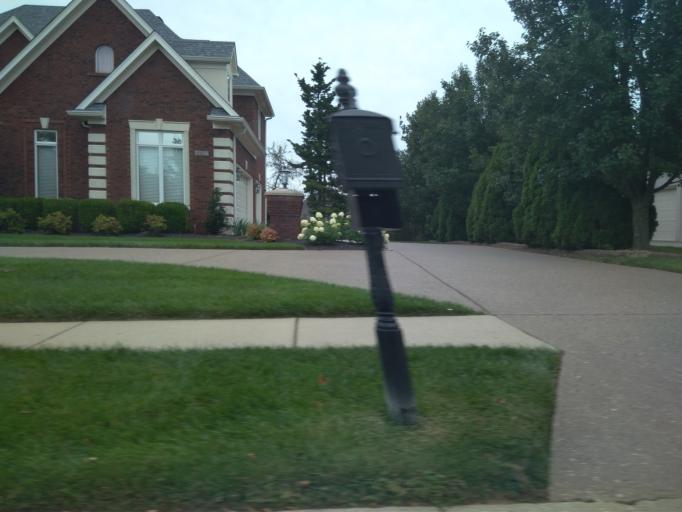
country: US
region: Kentucky
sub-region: Oldham County
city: Pewee Valley
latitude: 38.2713
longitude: -85.4806
